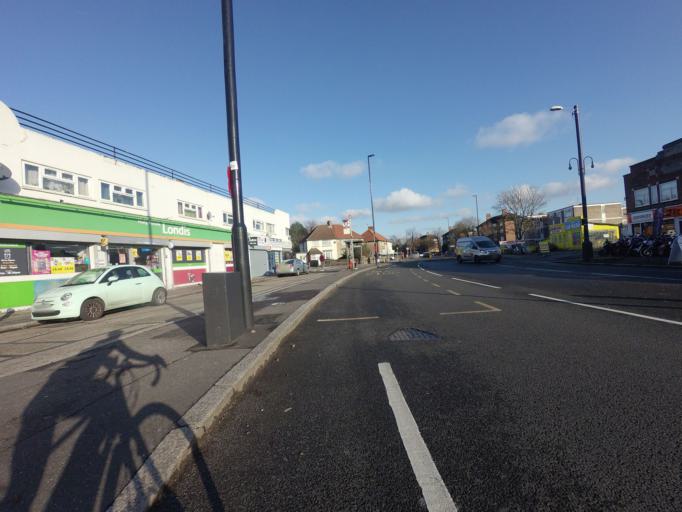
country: GB
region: England
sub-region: Greater London
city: Feltham
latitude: 51.4392
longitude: -0.4189
